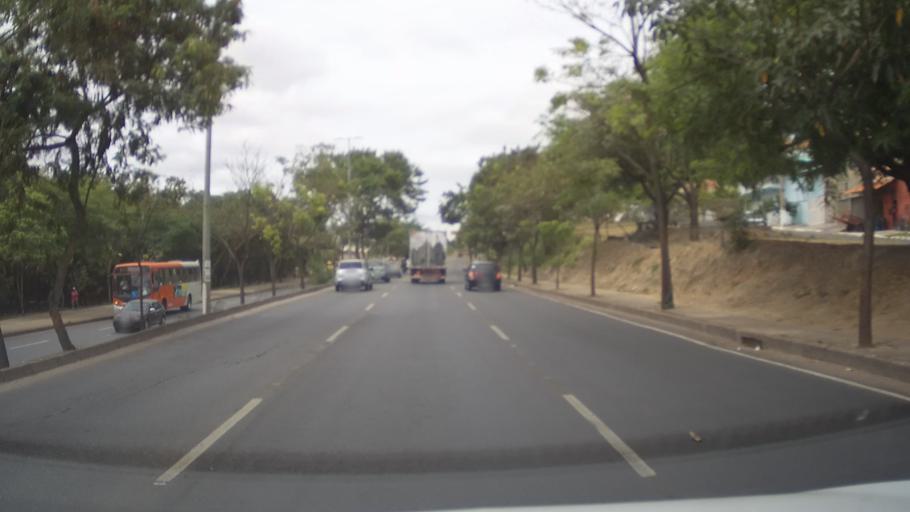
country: BR
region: Minas Gerais
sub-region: Belo Horizonte
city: Belo Horizonte
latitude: -19.8569
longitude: -43.9237
